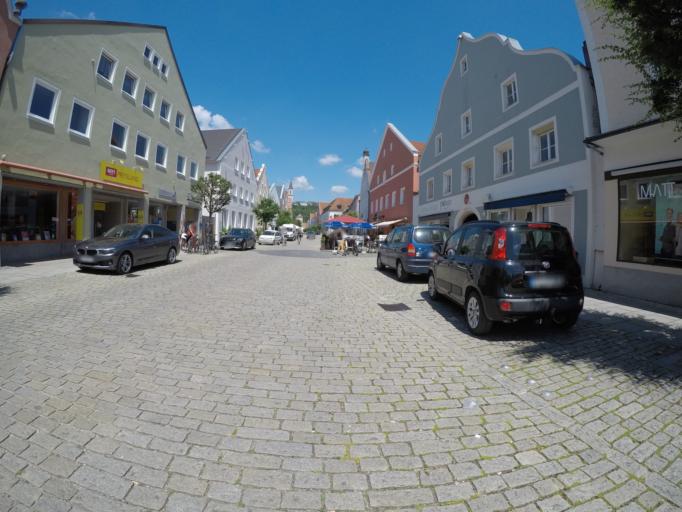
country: DE
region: Bavaria
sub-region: Lower Bavaria
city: Kelheim
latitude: 48.9176
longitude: 11.8717
